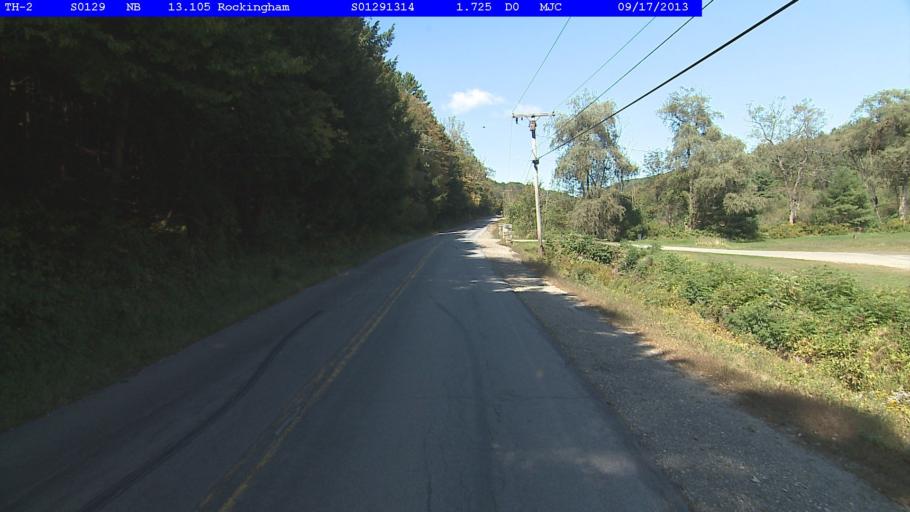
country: US
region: Vermont
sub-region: Windham County
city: Rockingham
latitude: 43.1423
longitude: -72.5179
